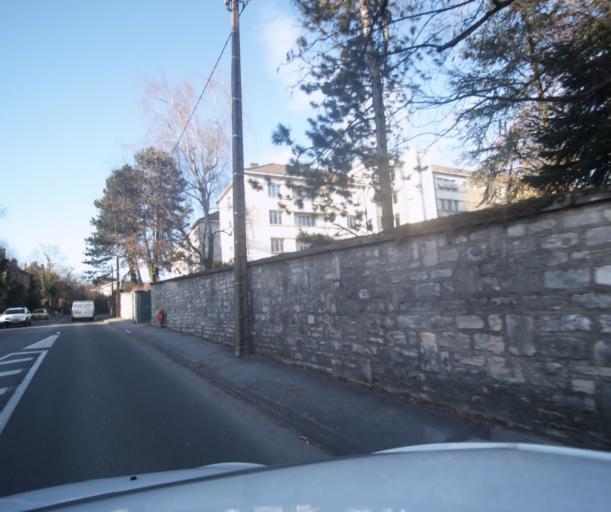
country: FR
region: Franche-Comte
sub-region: Departement du Doubs
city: Besancon
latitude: 47.2522
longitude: 6.0125
